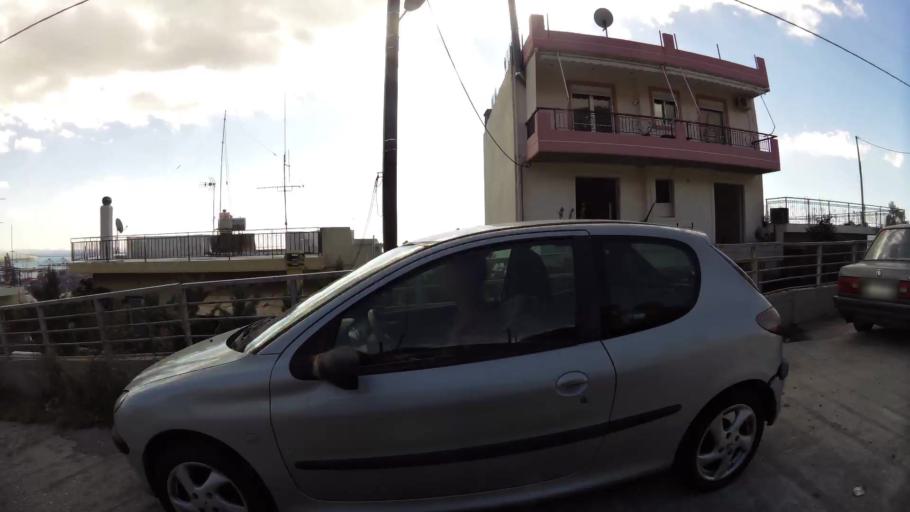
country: GR
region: Attica
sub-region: Nomos Piraios
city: Perama
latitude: 37.9675
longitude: 23.5781
